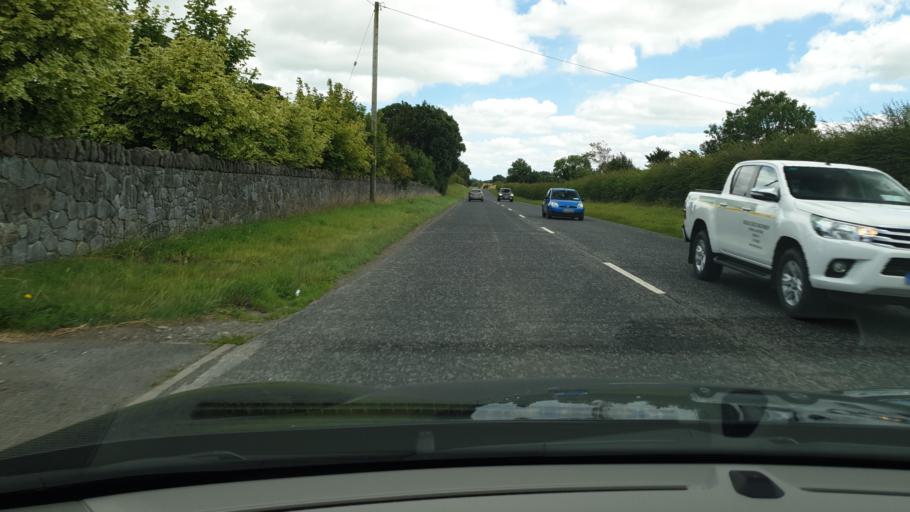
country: IE
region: Leinster
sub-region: An Mhi
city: Newtown Trim
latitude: 53.5342
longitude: -6.7029
